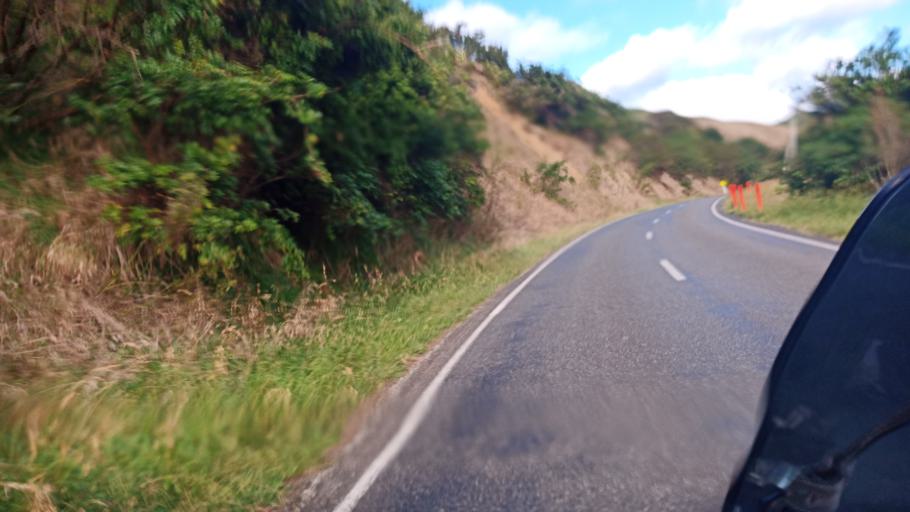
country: NZ
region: Gisborne
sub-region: Gisborne District
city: Gisborne
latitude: -38.5393
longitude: 177.5922
